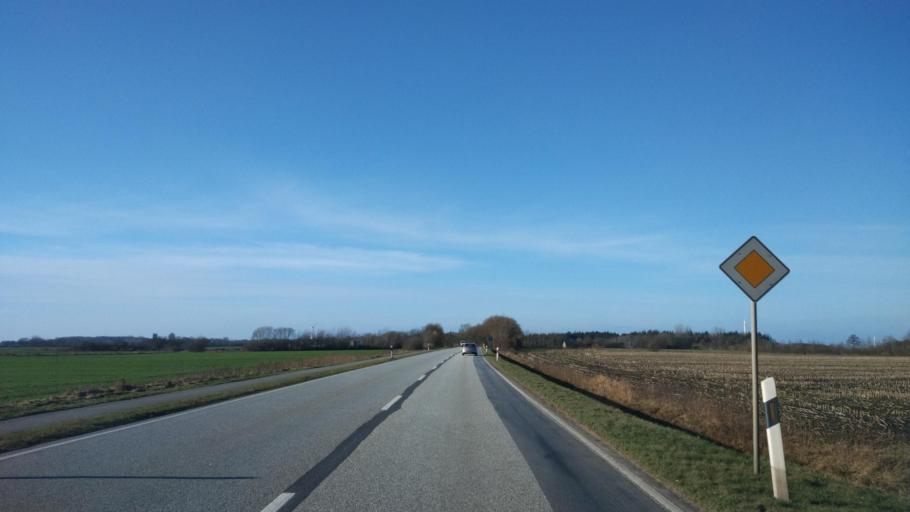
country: DE
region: Schleswig-Holstein
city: Silberstedt
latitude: 54.5167
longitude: 9.4056
